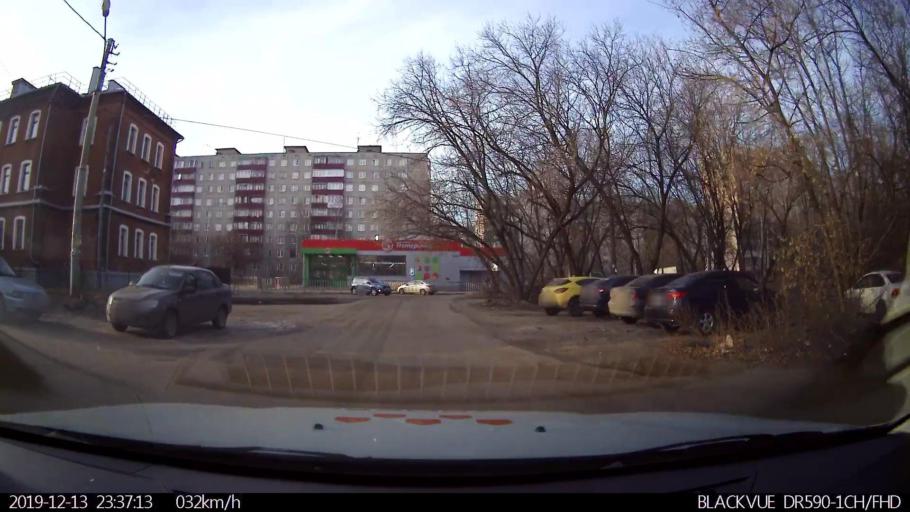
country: RU
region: Nizjnij Novgorod
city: Nizhniy Novgorod
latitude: 56.2933
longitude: 43.9429
